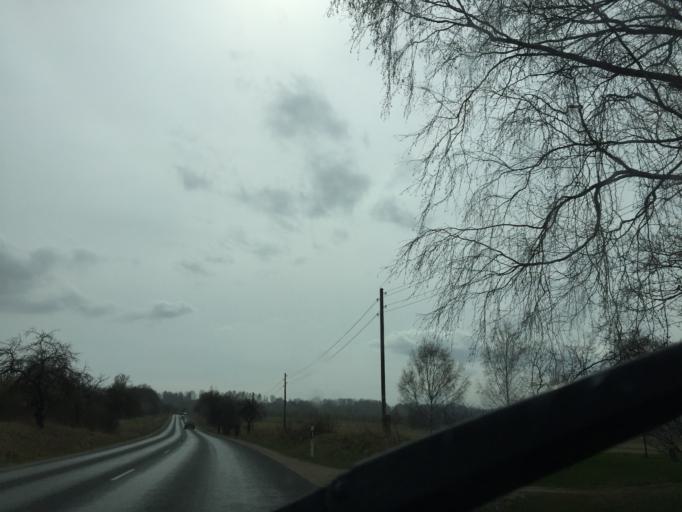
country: LV
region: Priekuli
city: Priekuli
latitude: 57.3416
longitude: 25.3361
